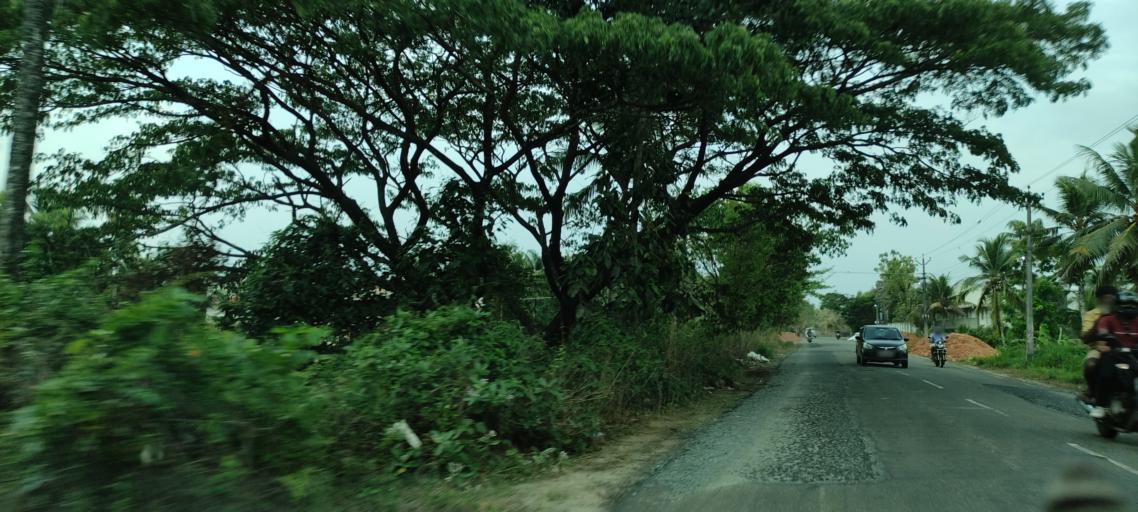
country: IN
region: Kerala
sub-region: Kottayam
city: Vaikam
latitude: 9.7463
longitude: 76.3634
